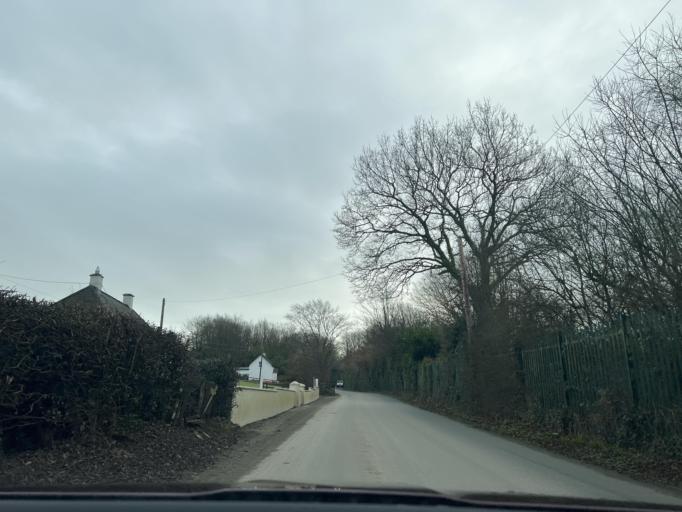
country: IE
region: Leinster
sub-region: Loch Garman
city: Castlebridge
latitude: 52.3828
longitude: -6.5606
